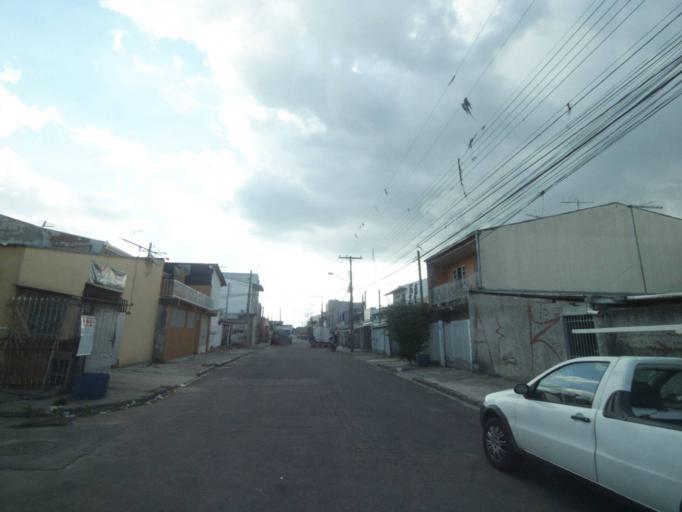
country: BR
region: Parana
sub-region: Sao Jose Dos Pinhais
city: Sao Jose dos Pinhais
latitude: -25.5321
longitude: -49.2728
